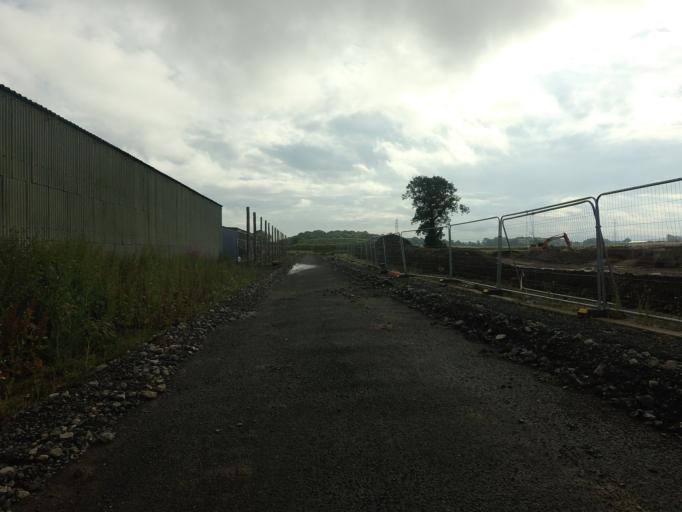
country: GB
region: Scotland
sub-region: West Lothian
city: East Calder
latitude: 55.9037
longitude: -3.4401
